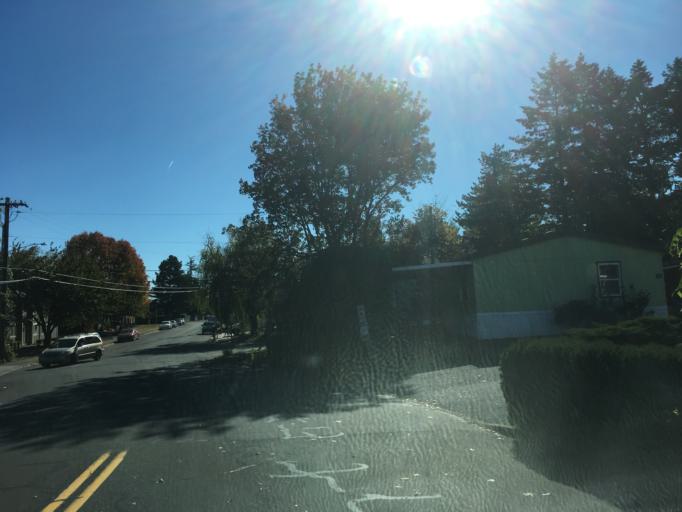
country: US
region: Oregon
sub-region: Multnomah County
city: Gresham
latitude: 45.4937
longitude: -122.4100
